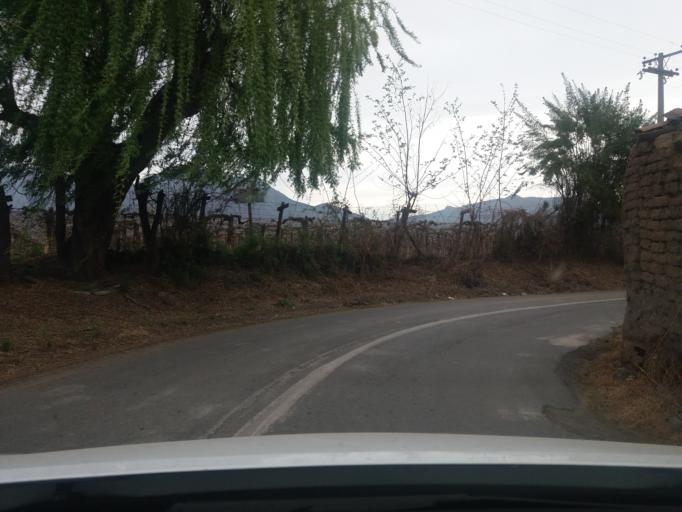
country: CL
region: Valparaiso
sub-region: Provincia de Los Andes
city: Los Andes
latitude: -32.8530
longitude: -70.6401
